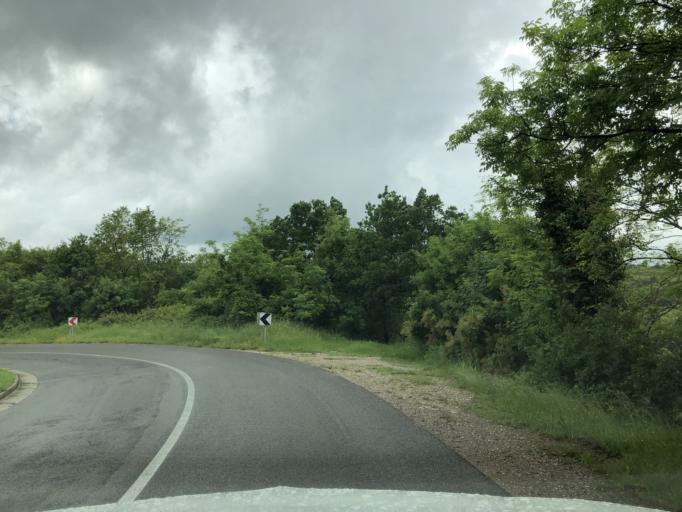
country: SI
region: Koper-Capodistria
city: Prade
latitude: 45.5041
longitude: 13.7756
